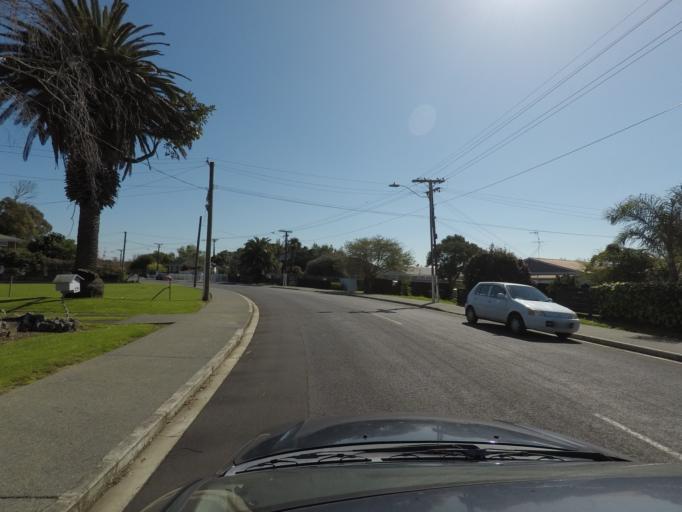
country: NZ
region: Auckland
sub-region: Auckland
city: Tamaki
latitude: -36.9256
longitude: 174.8617
